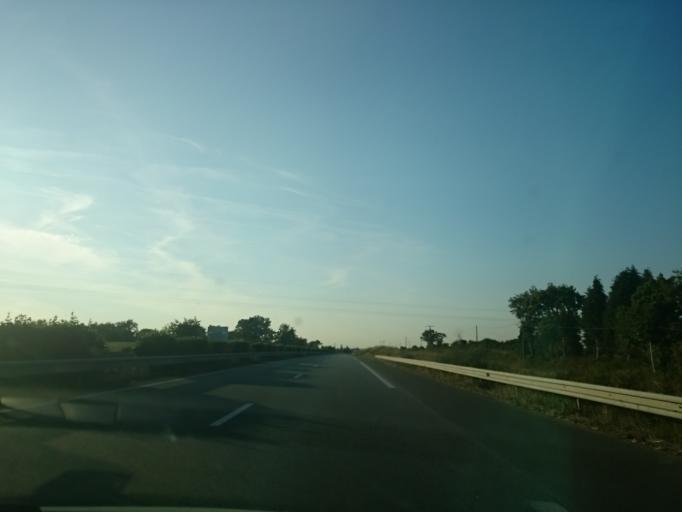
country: FR
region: Brittany
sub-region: Departement du Morbihan
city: Theix
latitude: 47.6186
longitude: -2.6249
